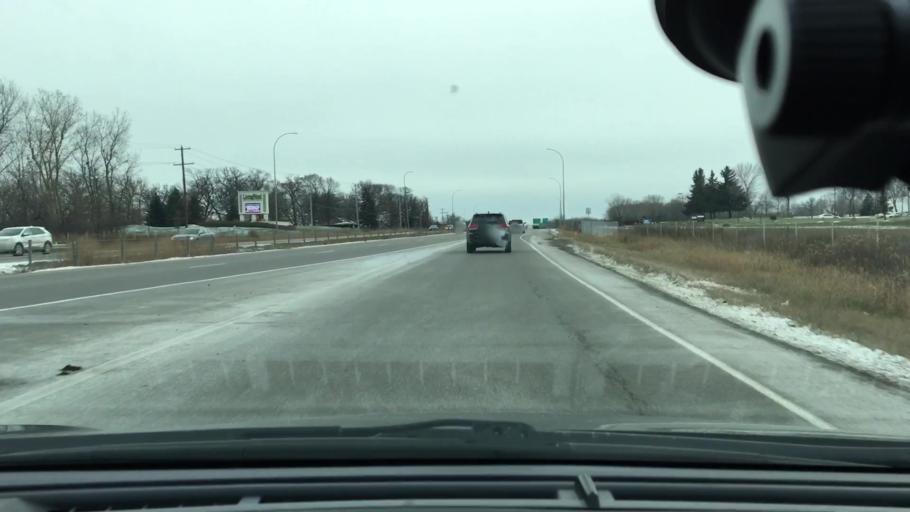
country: US
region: Minnesota
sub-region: Hennepin County
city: Osseo
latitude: 45.0912
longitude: -93.4026
